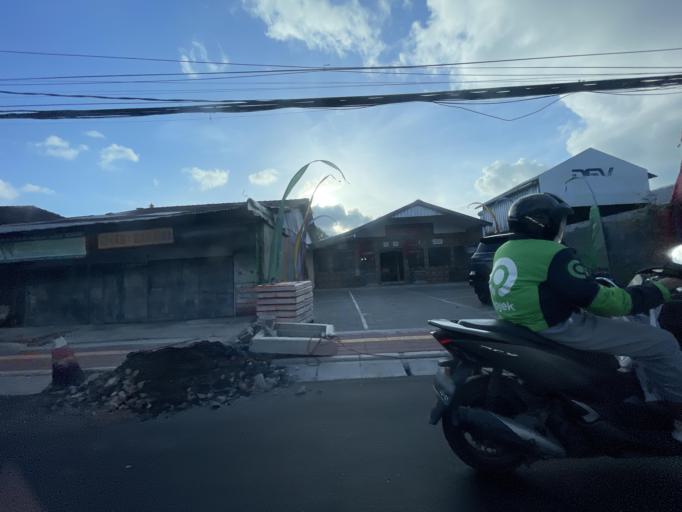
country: ID
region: Bali
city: Kelanabian
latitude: -8.7588
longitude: 115.1791
